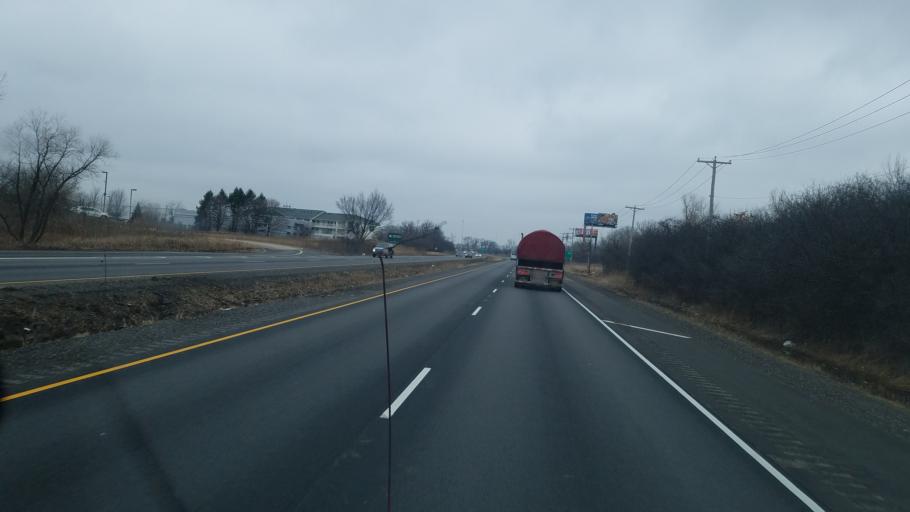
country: US
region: Illinois
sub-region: Lake County
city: Park City
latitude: 42.3357
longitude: -87.8851
